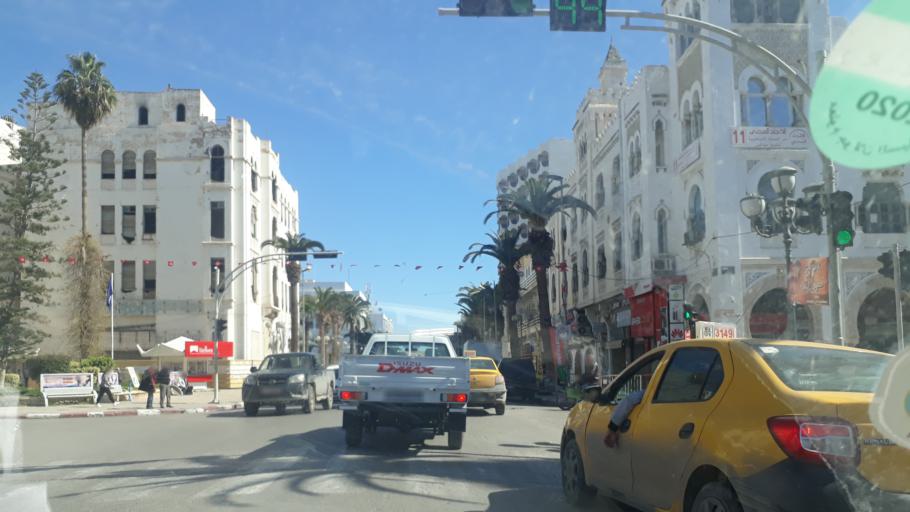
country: TN
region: Safaqis
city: Sfax
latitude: 34.7326
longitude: 10.7639
